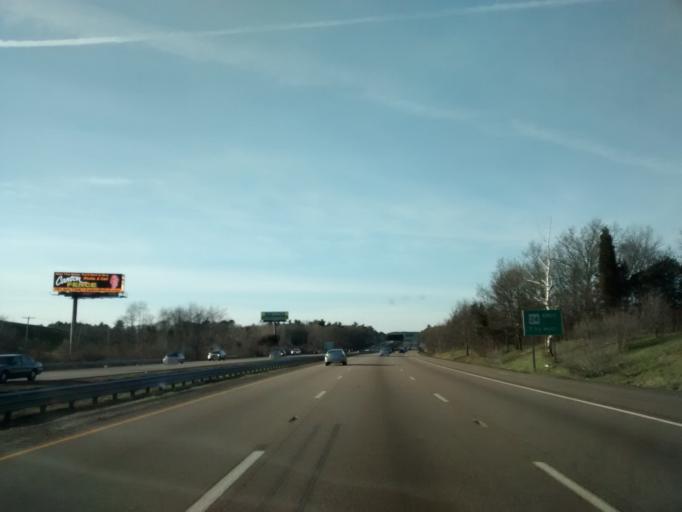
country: US
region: Massachusetts
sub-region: Norfolk County
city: Randolph
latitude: 42.1768
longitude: -71.0748
